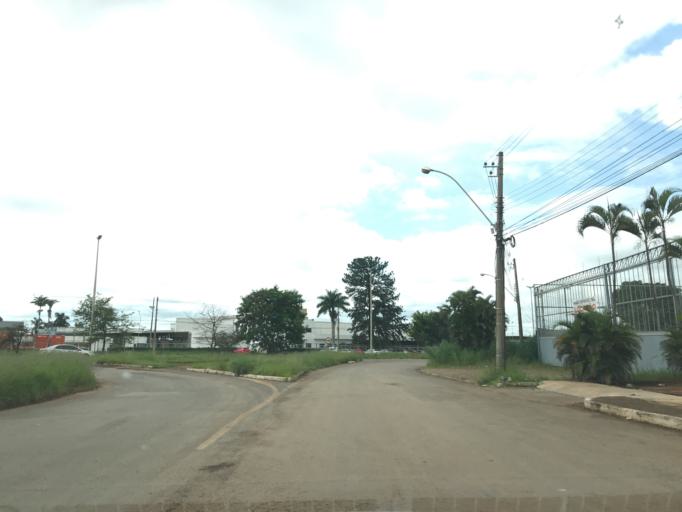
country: BR
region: Federal District
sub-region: Brasilia
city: Brasilia
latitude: -15.7938
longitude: -47.9894
